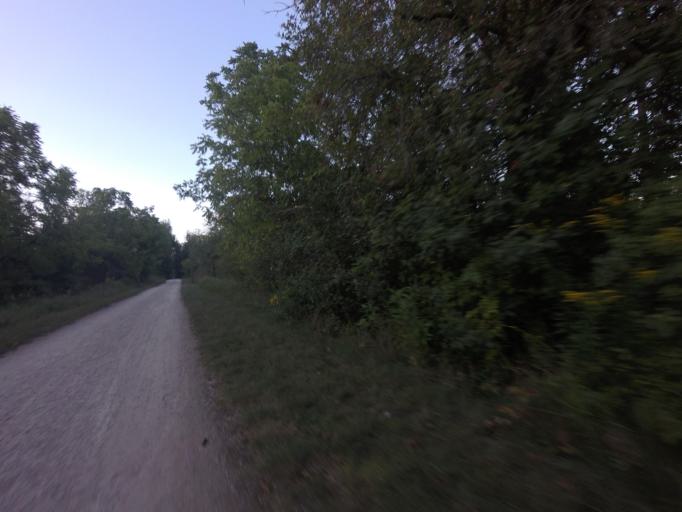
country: CA
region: Ontario
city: Brampton
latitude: 43.9163
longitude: -79.8410
